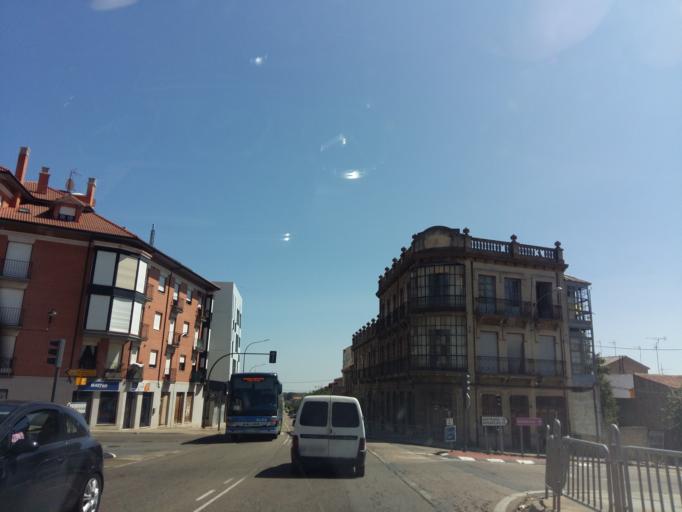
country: ES
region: Castille and Leon
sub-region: Provincia de Leon
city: Astorga
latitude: 42.4560
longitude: -6.0609
